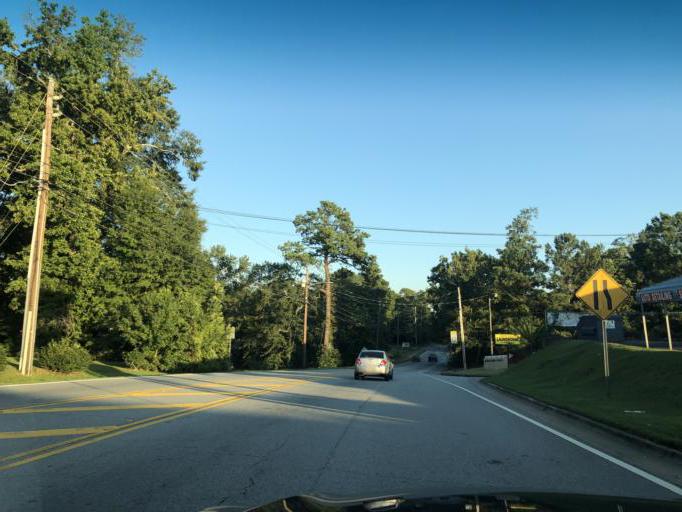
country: US
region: Georgia
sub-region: Muscogee County
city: Columbus
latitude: 32.5217
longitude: -84.8876
